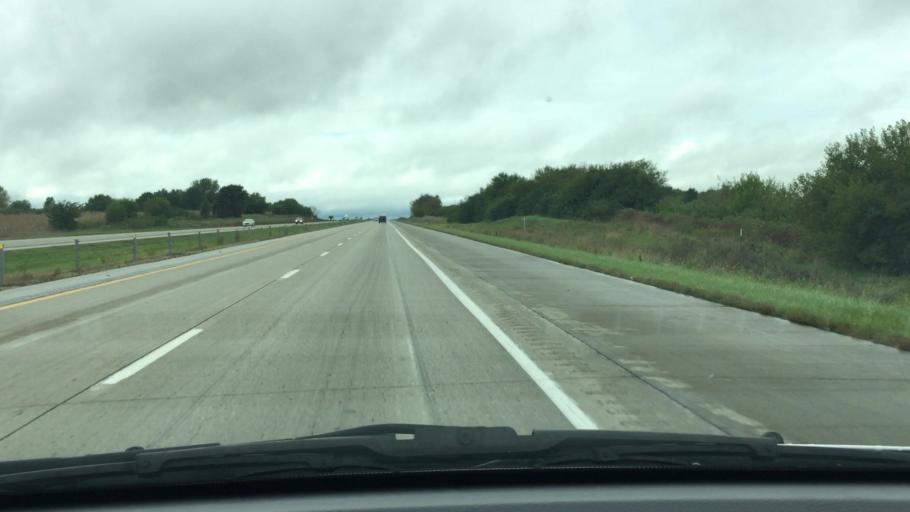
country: US
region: Iowa
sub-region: Polk County
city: Bondurant
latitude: 41.6772
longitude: -93.4176
